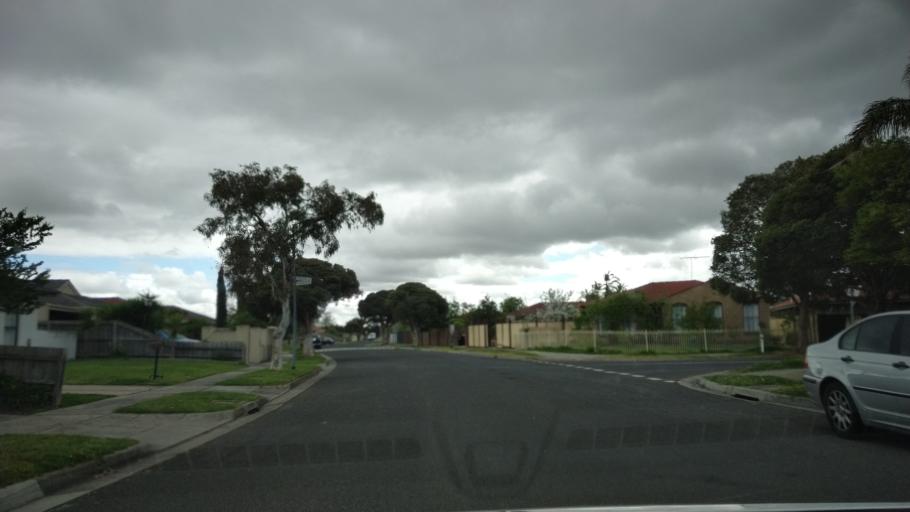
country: AU
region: Victoria
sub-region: Greater Dandenong
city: Keysborough
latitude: -37.9926
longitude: 145.1654
